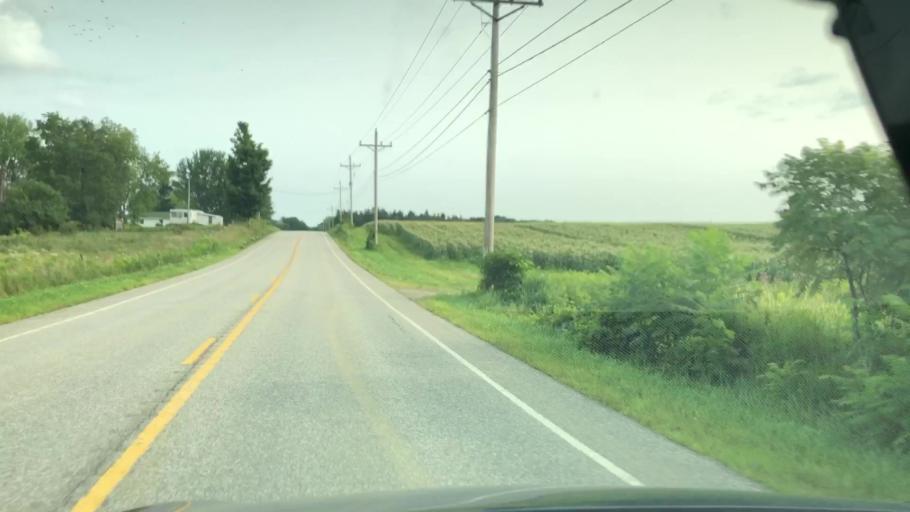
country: US
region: Pennsylvania
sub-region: Erie County
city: Union City
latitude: 41.9346
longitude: -79.8439
